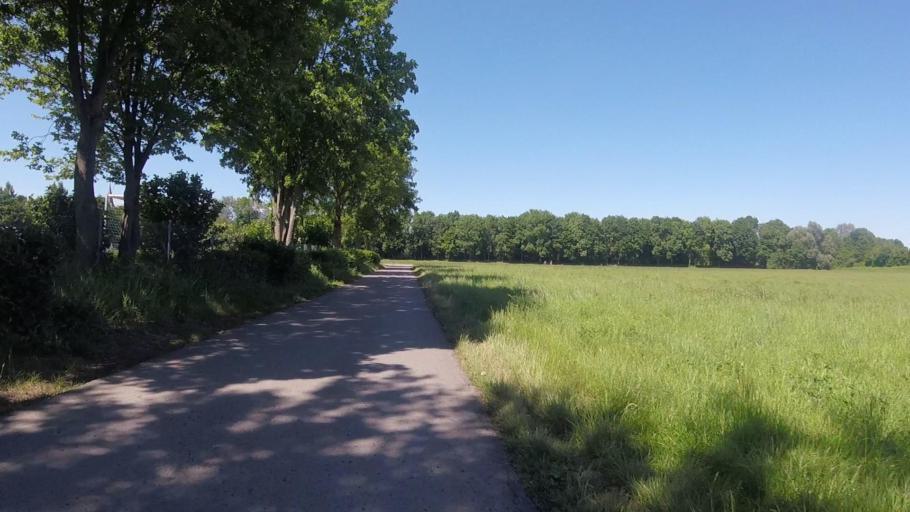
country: DE
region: Baden-Wuerttemberg
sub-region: Regierungsbezirk Stuttgart
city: Murr
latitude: 48.9607
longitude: 9.2636
